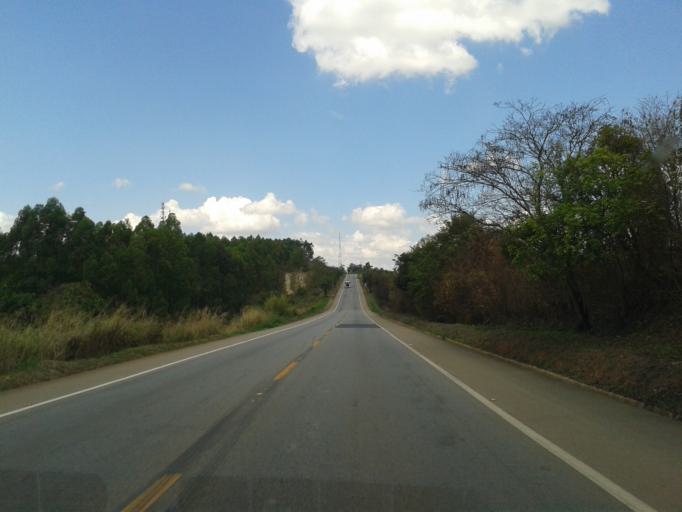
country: BR
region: Minas Gerais
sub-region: Campos Altos
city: Campos Altos
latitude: -19.7451
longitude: -45.9570
